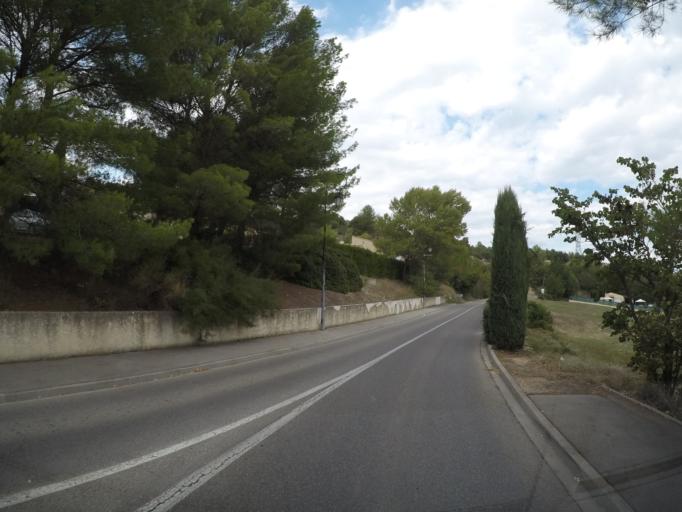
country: FR
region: Provence-Alpes-Cote d'Azur
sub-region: Departement des Alpes-de-Haute-Provence
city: Greoux-les-Bains
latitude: 43.7630
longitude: 5.8892
